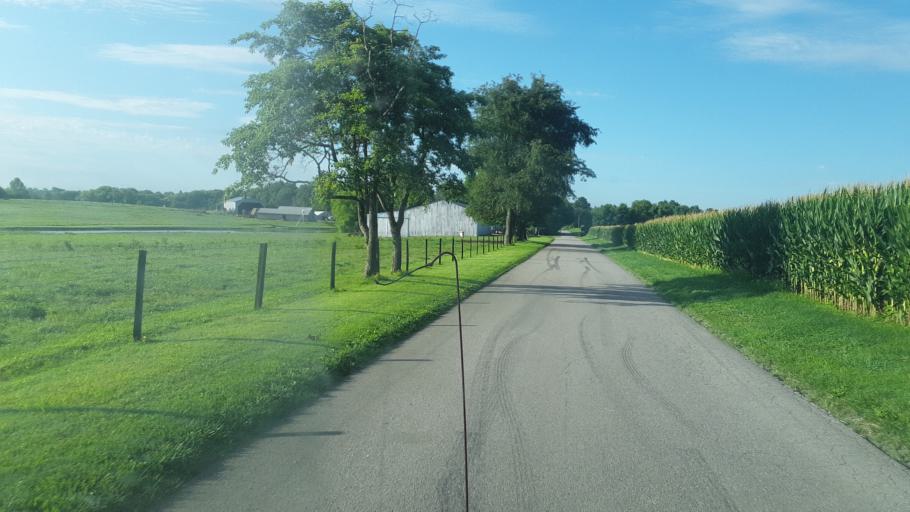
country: US
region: Kentucky
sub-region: Todd County
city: Guthrie
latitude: 36.6798
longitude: -87.1688
